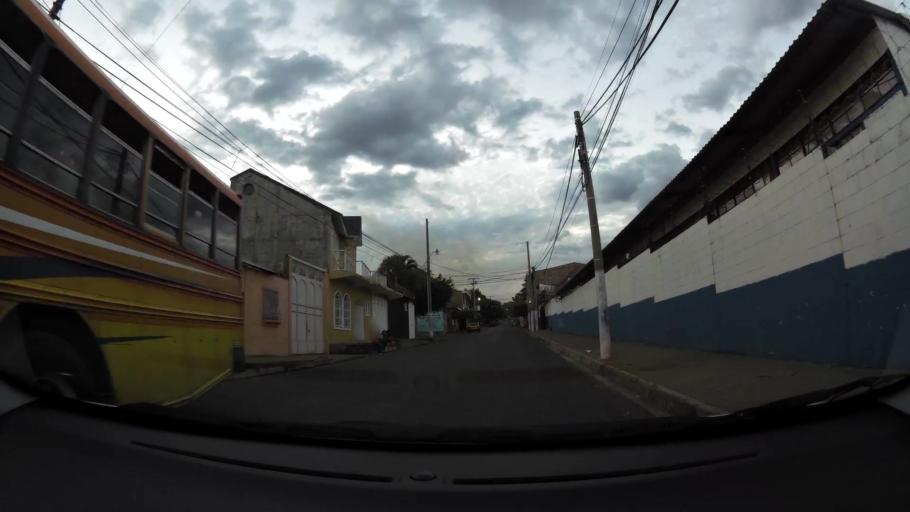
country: SV
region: San Vicente
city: San Vicente
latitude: 13.6415
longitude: -88.7897
